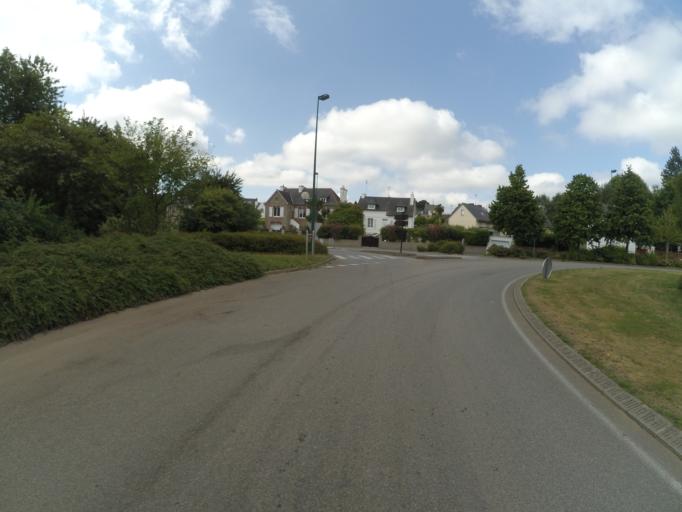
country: FR
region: Brittany
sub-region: Departement du Finistere
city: Rosporden
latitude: 47.9582
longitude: -3.8198
